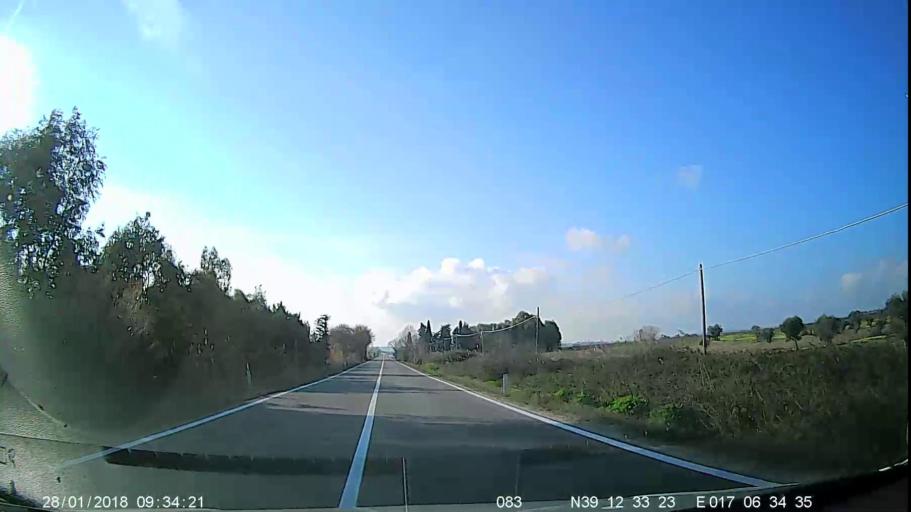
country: IT
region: Calabria
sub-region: Provincia di Crotone
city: Tronca
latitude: 39.2087
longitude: 17.1093
